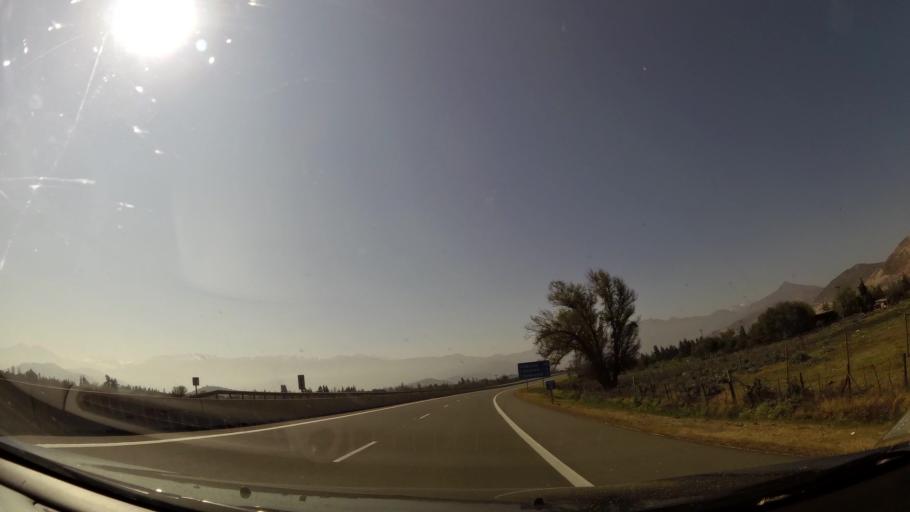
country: CL
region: Santiago Metropolitan
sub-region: Provincia de Chacabuco
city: Chicureo Abajo
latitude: -33.2916
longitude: -70.6963
